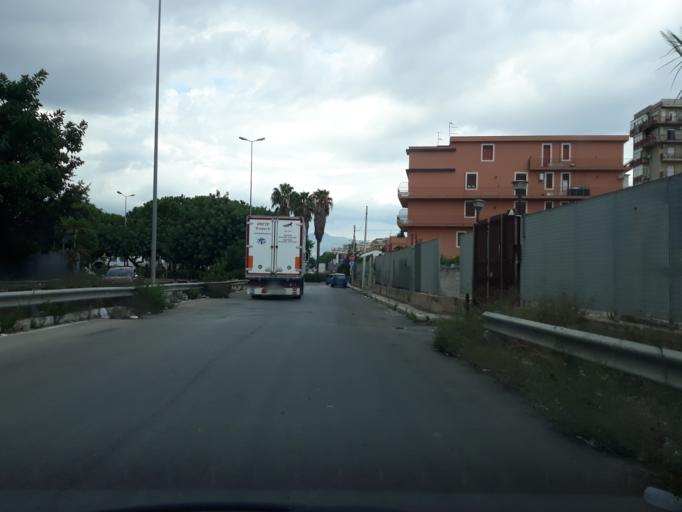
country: IT
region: Sicily
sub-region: Palermo
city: Ciaculli
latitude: 38.0936
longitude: 13.4041
